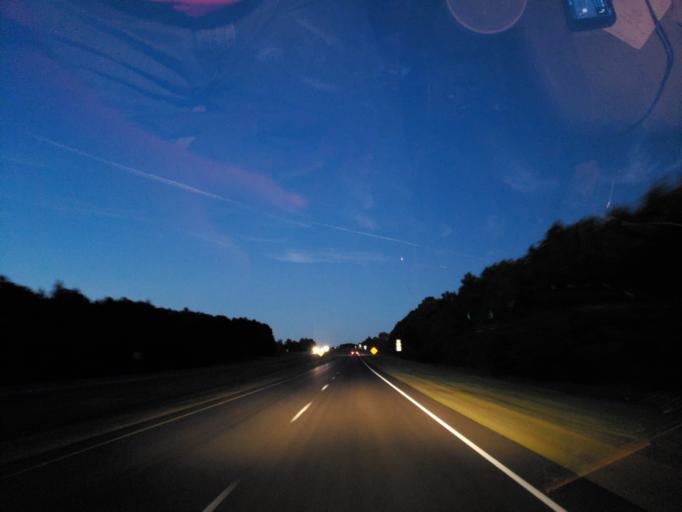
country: US
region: Mississippi
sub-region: Clarke County
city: Quitman
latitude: 32.0344
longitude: -88.6804
